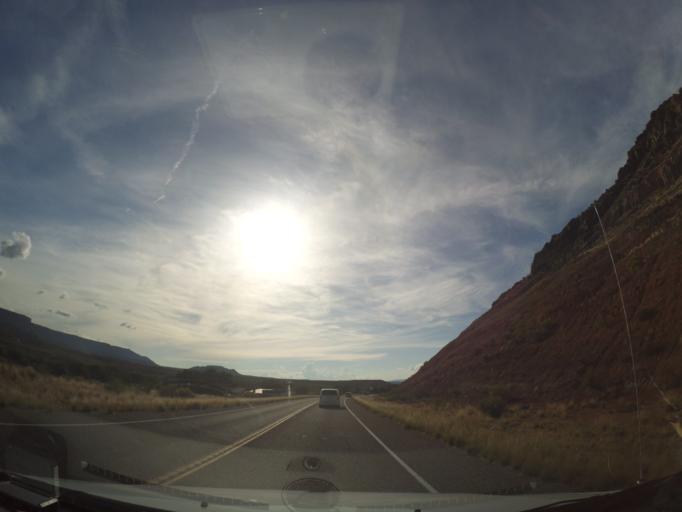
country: US
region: Utah
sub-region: Washington County
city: LaVerkin
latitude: 37.1952
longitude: -113.1521
